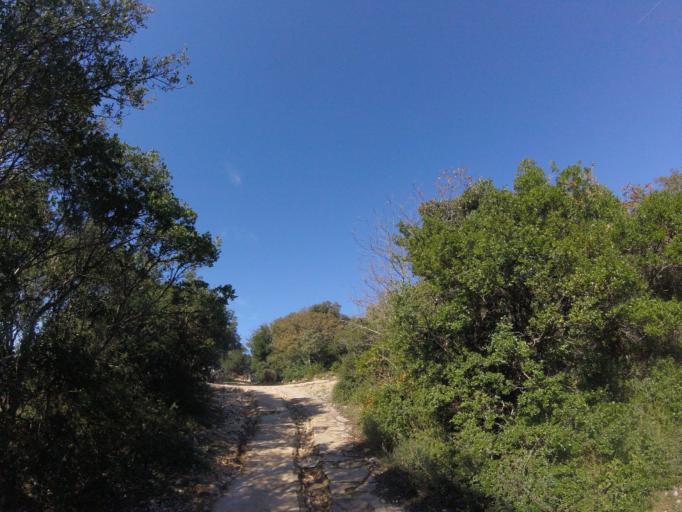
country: HR
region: Istarska
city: Vrsar
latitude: 45.1357
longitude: 13.6541
